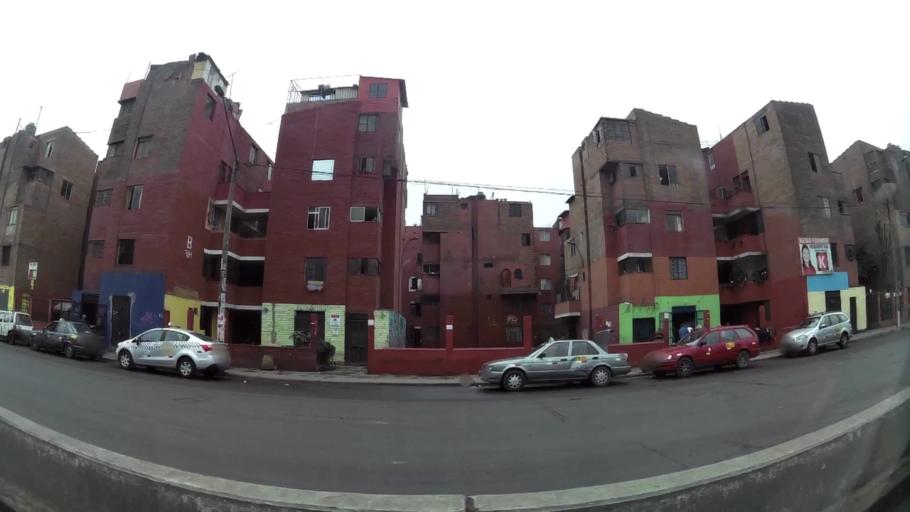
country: PE
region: Lima
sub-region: Lima
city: San Luis
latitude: -12.0667
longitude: -77.0175
